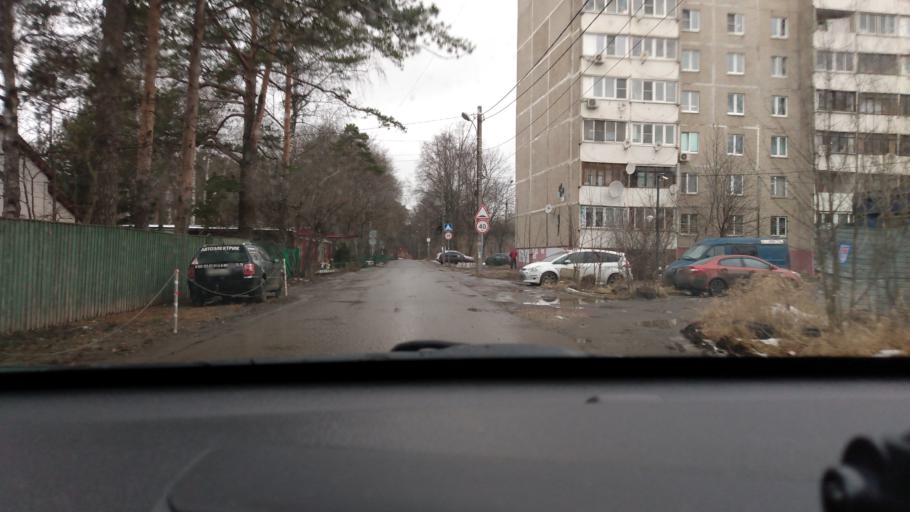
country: RU
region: Moskovskaya
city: Druzhba
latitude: 55.8989
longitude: 37.7509
